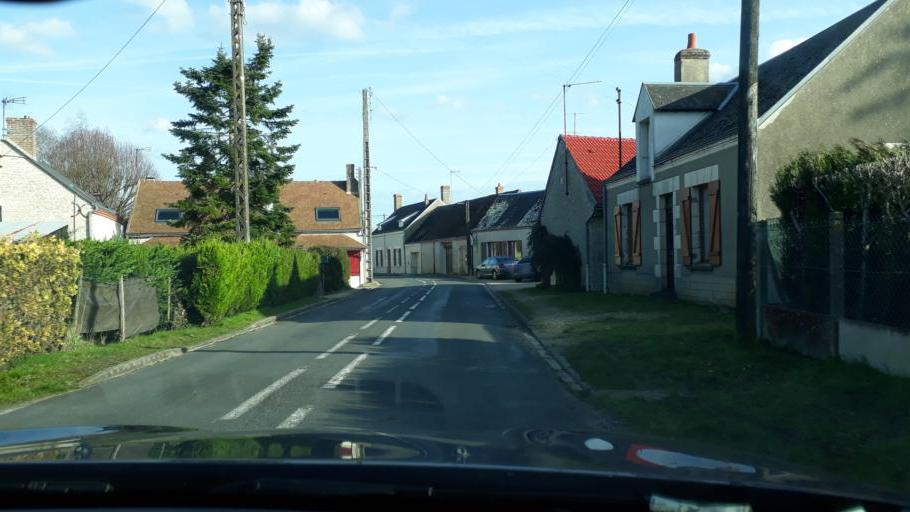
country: FR
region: Centre
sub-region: Departement du Loiret
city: Chilleurs-aux-Bois
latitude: 48.0632
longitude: 2.2119
